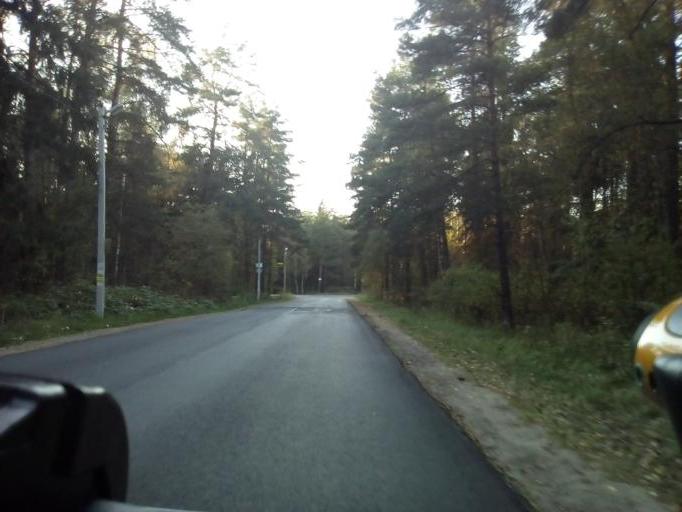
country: RU
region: Moskovskaya
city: Ramenskoye
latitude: 55.6137
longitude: 38.2798
